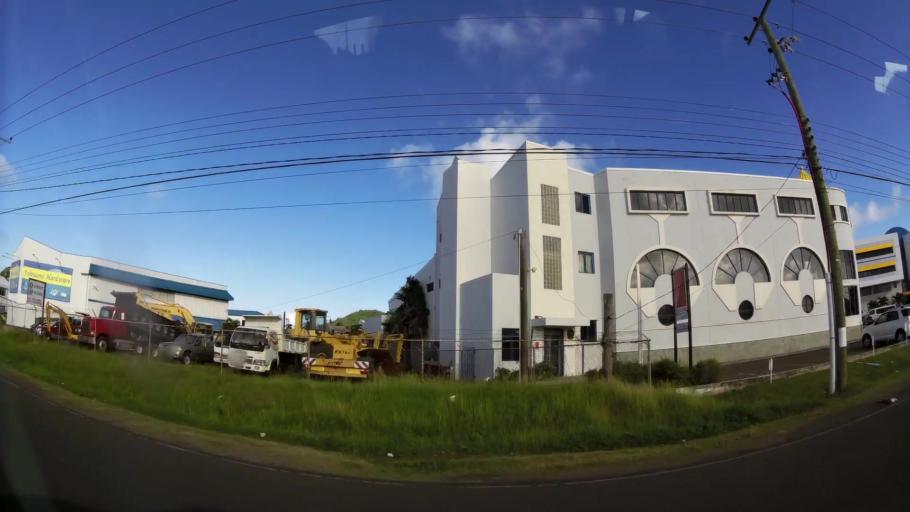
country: LC
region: Gros-Islet
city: Gros Islet
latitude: 14.0768
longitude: -60.9477
